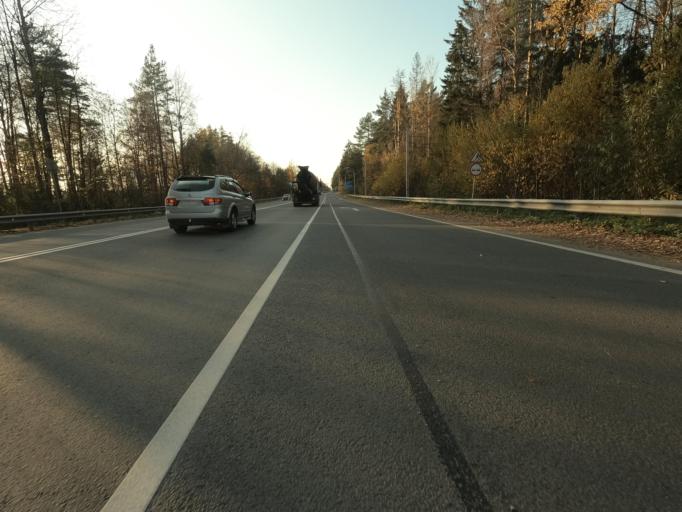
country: RU
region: St.-Petersburg
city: Pesochnyy
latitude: 60.1806
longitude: 30.1370
